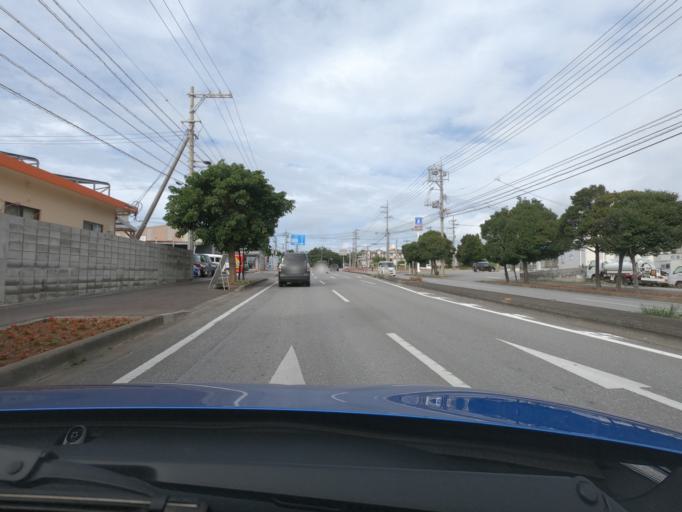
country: JP
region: Okinawa
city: Nago
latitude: 26.6770
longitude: 127.8914
